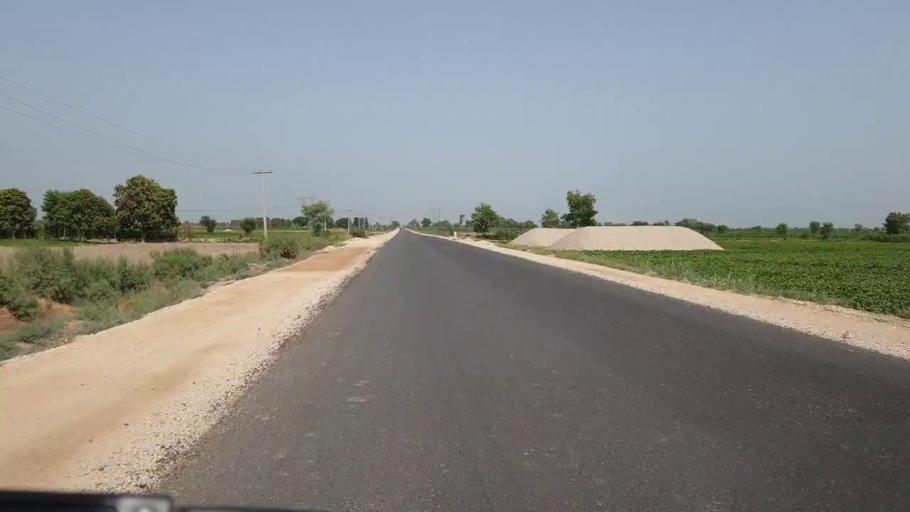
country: PK
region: Sindh
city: Sakrand
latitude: 26.2568
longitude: 68.1939
